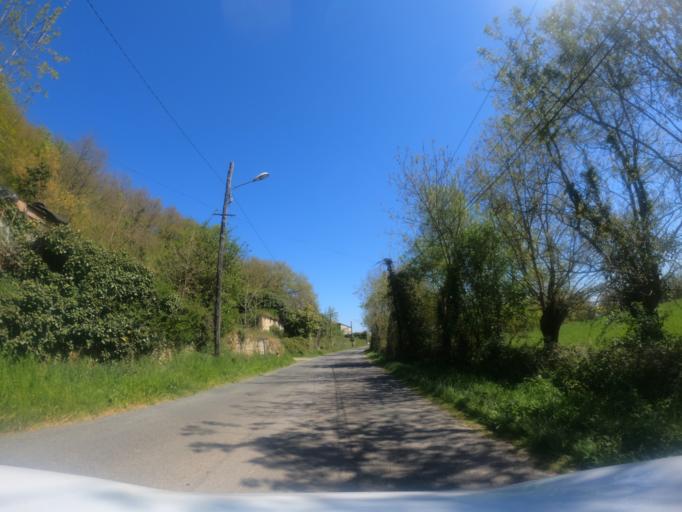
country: FR
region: Pays de la Loire
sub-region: Departement de la Vendee
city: Fontenay-le-Comte
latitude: 46.4433
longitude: -0.8527
